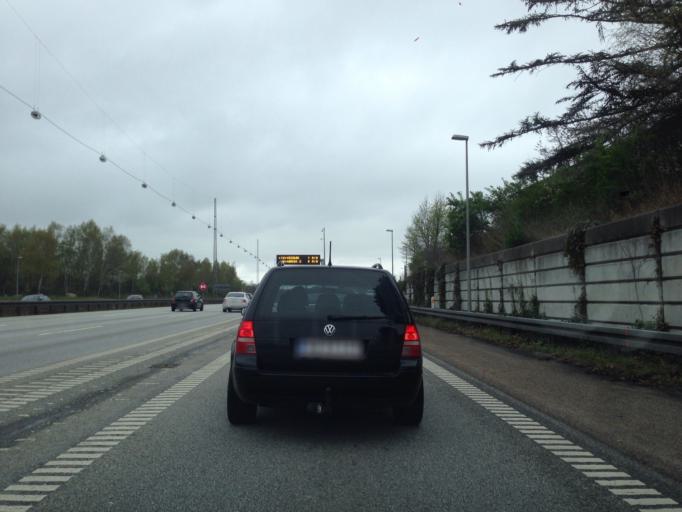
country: DK
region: Capital Region
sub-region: Rudersdal Kommune
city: Trorod
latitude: 55.8156
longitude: 12.5285
